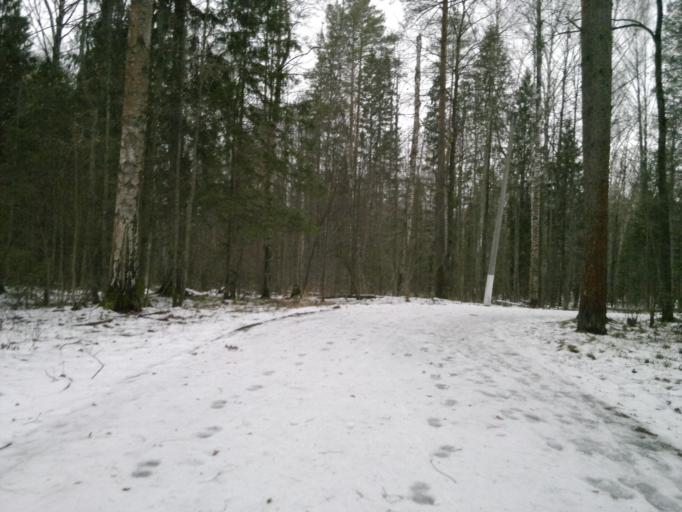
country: RU
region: Mariy-El
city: Yoshkar-Ola
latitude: 56.6022
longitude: 47.9627
